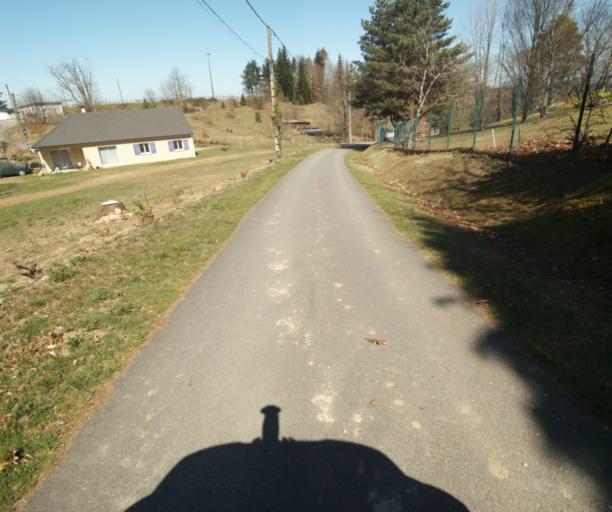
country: FR
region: Limousin
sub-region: Departement de la Correze
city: Saint-Mexant
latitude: 45.2753
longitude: 1.6610
